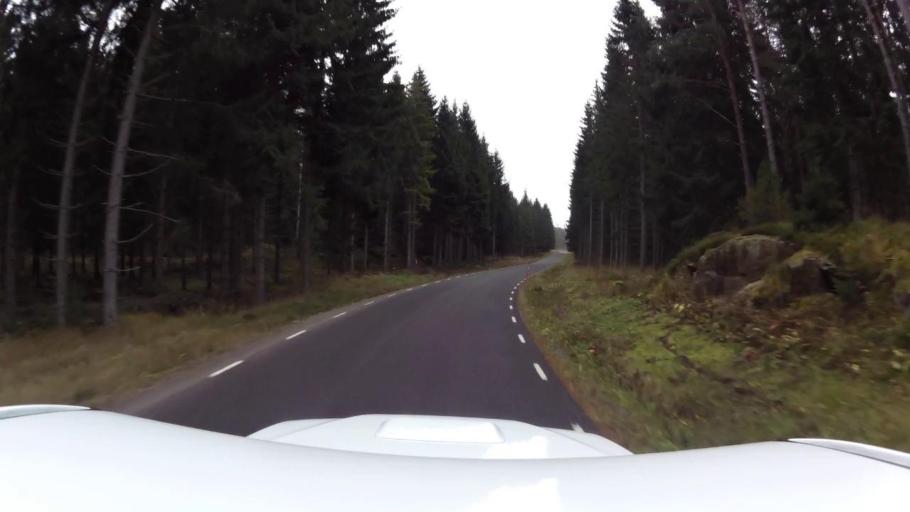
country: SE
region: OEstergoetland
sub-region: Kinda Kommun
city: Rimforsa
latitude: 58.1585
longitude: 15.5079
